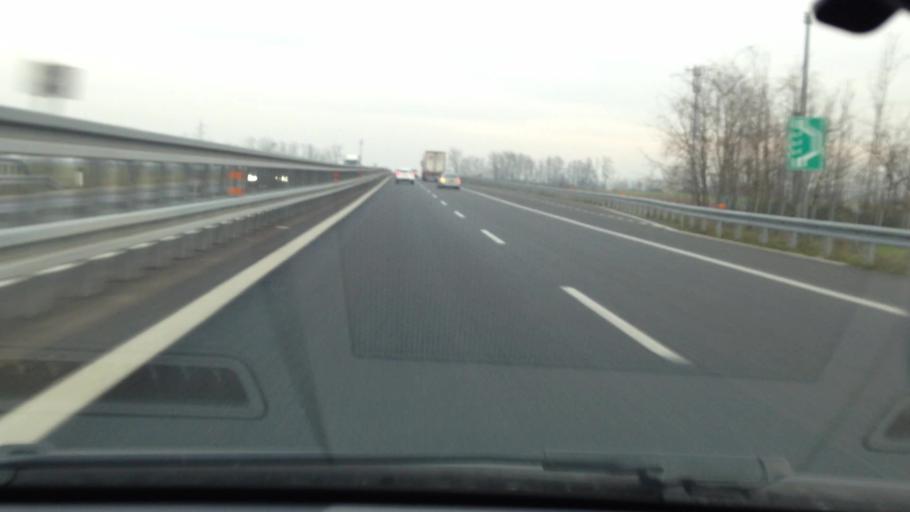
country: IT
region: Piedmont
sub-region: Provincia di Alessandria
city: Solero
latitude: 44.9265
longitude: 8.5026
